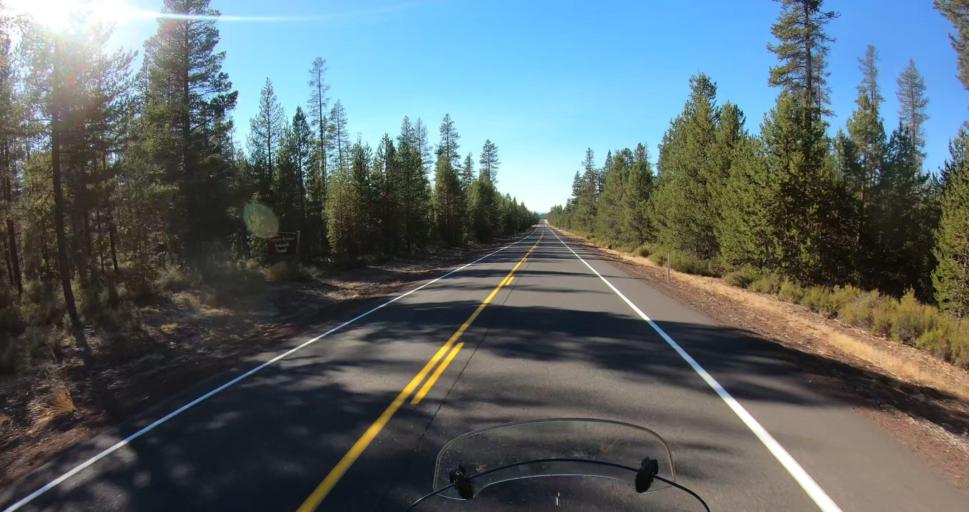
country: US
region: Oregon
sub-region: Deschutes County
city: La Pine
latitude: 43.4477
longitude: -121.3520
